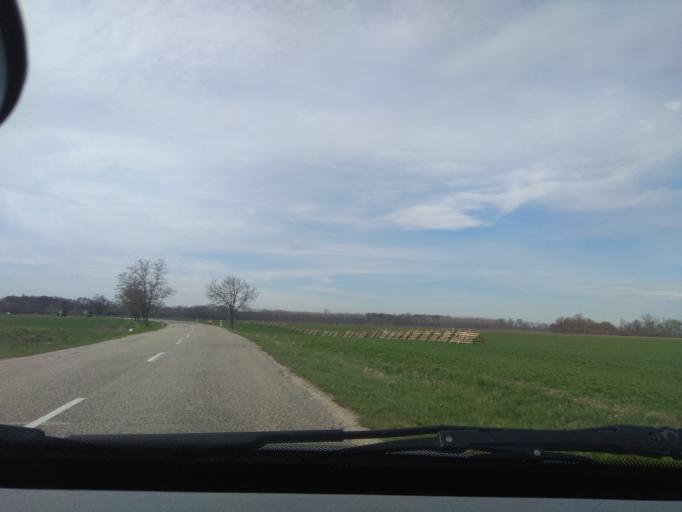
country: SK
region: Trnavsky
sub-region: Okres Dunajska Streda
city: Velky Meder
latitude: 47.8277
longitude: 17.7513
